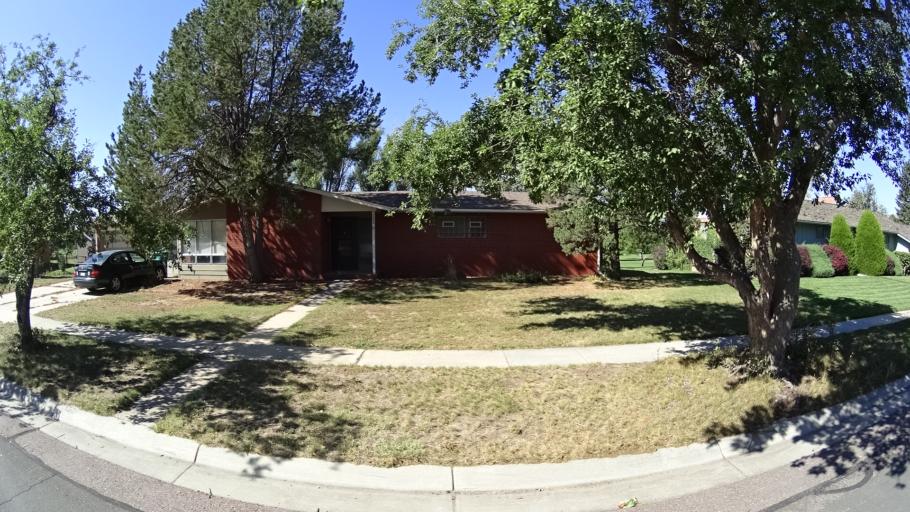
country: US
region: Colorado
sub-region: El Paso County
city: Colorado Springs
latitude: 38.8723
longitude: -104.7827
